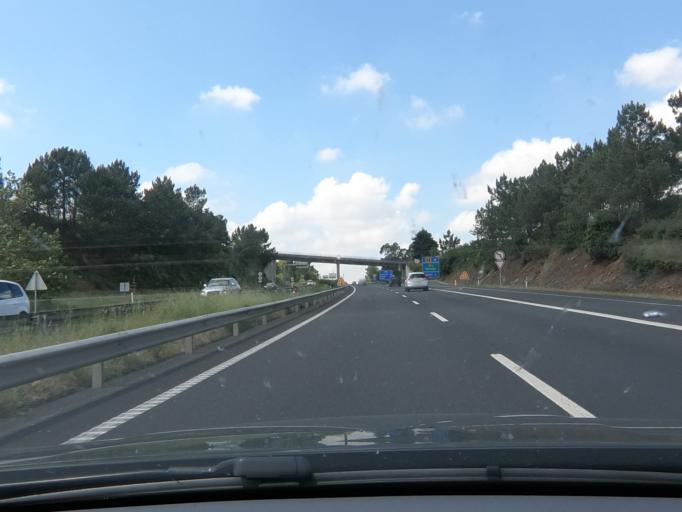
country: PT
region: Leiria
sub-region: Obidos
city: Obidos
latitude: 39.3525
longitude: -9.1526
